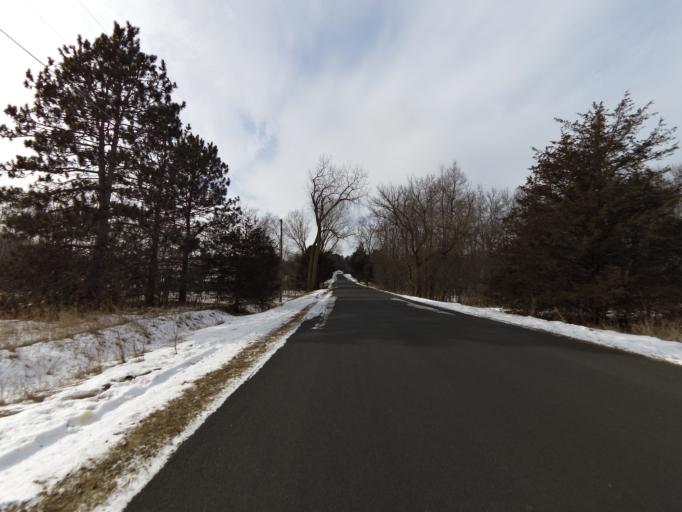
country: US
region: Minnesota
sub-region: Washington County
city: Lake Saint Croix Beach
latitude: 44.9143
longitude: -92.7683
